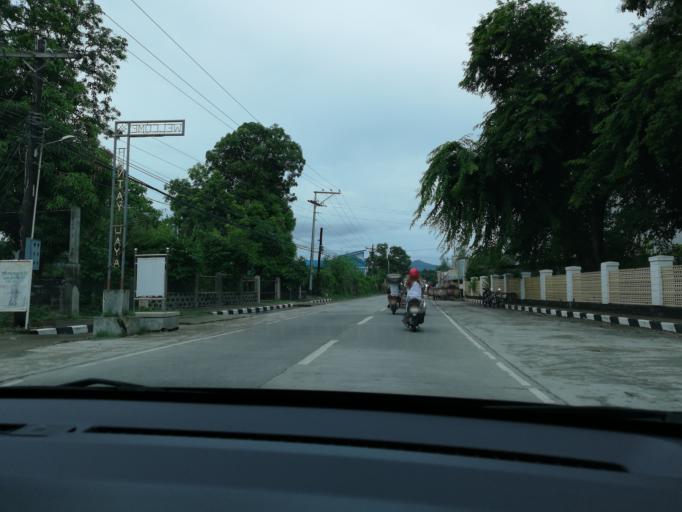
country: PH
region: Ilocos
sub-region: Province of Ilocos Sur
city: Vigan
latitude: 17.5786
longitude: 120.3794
